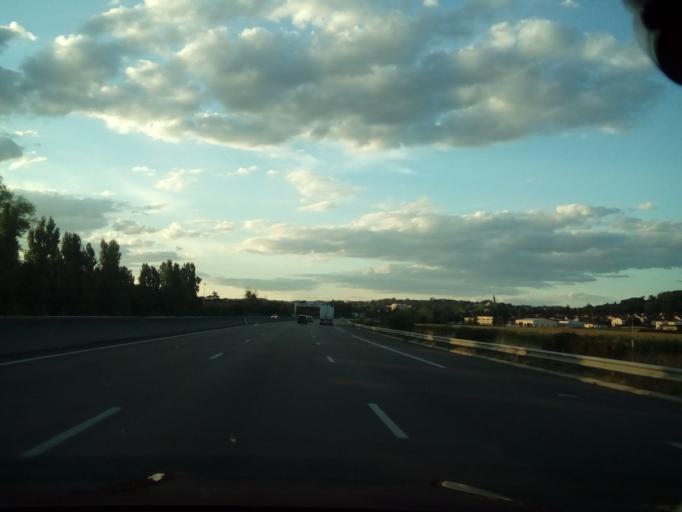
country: FR
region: Rhone-Alpes
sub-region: Departement de l'Isere
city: Salaise-sur-Sanne
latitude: 45.3524
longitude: 4.8056
